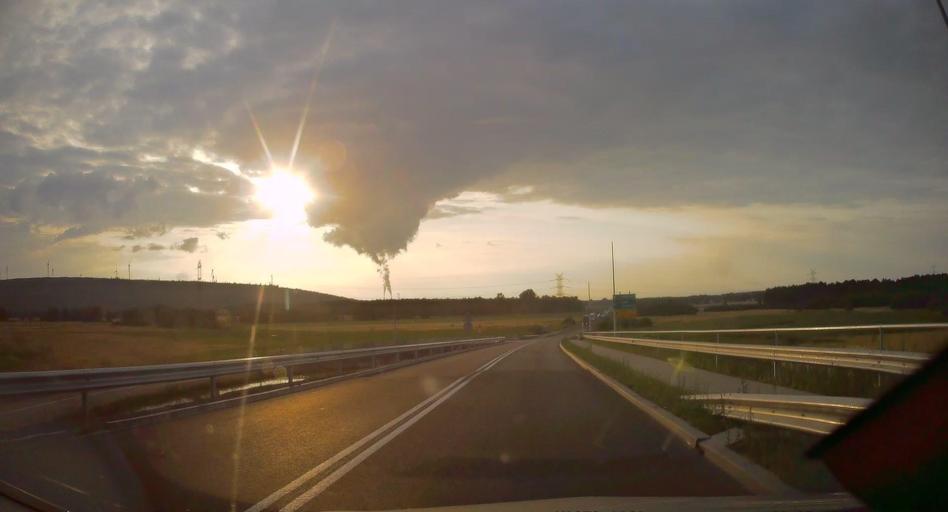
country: PL
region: Lodz Voivodeship
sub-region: Powiat radomszczanski
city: Kamiensk
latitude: 51.2131
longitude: 19.4851
